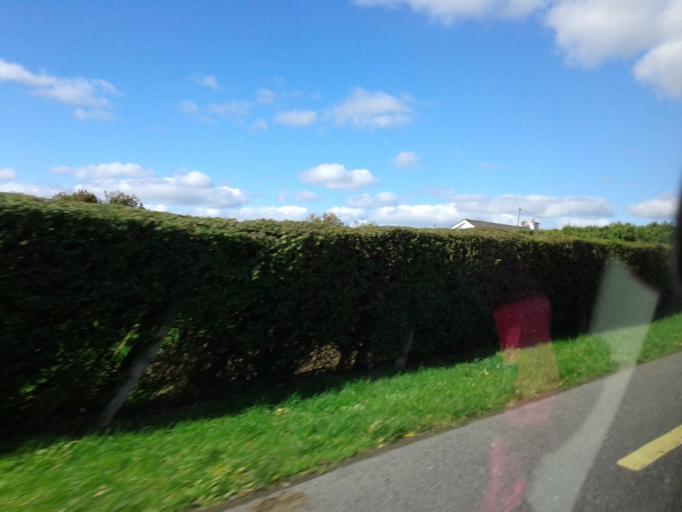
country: IE
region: Leinster
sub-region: An Mhi
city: Slane
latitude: 53.6840
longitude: -6.5414
